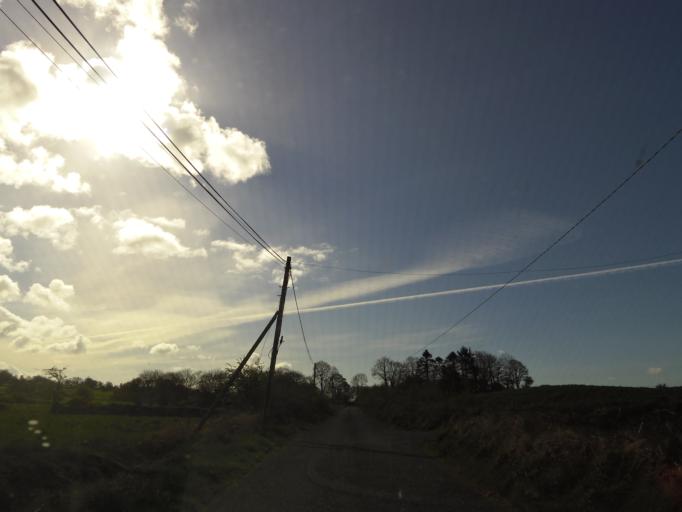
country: IE
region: Connaught
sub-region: Maigh Eo
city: Kiltamagh
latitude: 53.7992
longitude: -8.9691
